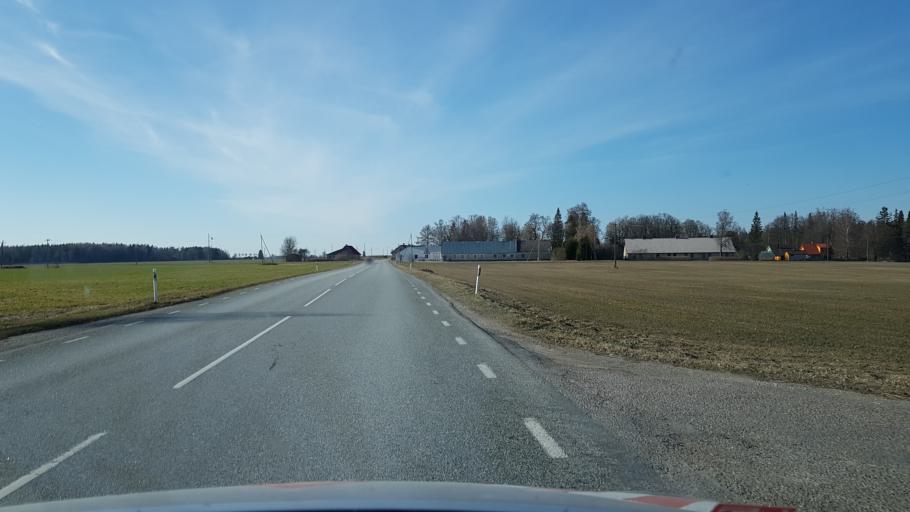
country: EE
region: Laeaene-Virumaa
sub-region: Vinni vald
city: Vinni
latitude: 59.2040
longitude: 26.5585
